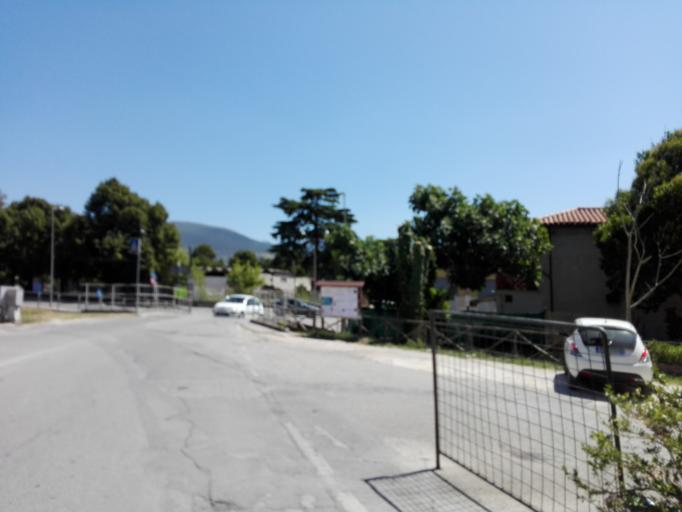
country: IT
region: Umbria
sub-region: Provincia di Perugia
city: Foligno
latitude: 42.9499
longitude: 12.6927
